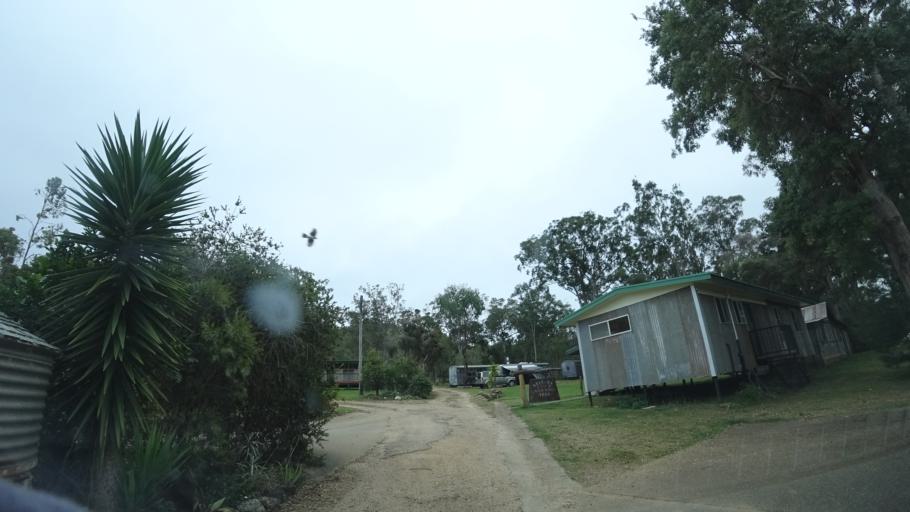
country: AU
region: Queensland
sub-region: Tablelands
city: Atherton
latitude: -17.3676
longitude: 145.3892
